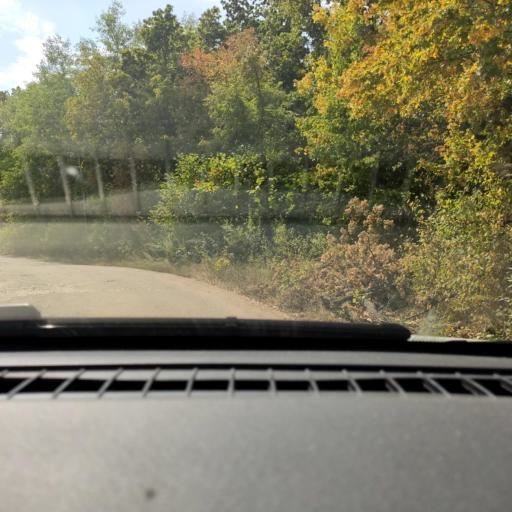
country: RU
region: Voronezj
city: Pridonskoy
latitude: 51.7550
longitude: 39.0785
